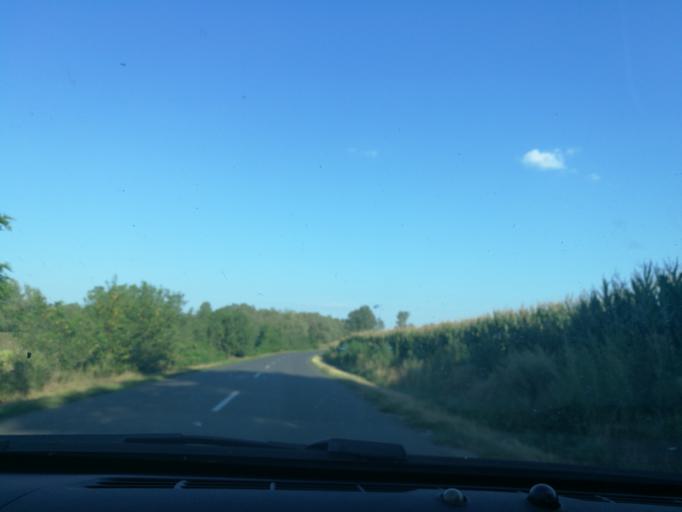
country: HU
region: Szabolcs-Szatmar-Bereg
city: Tiszabercel
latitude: 48.1519
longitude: 21.6135
